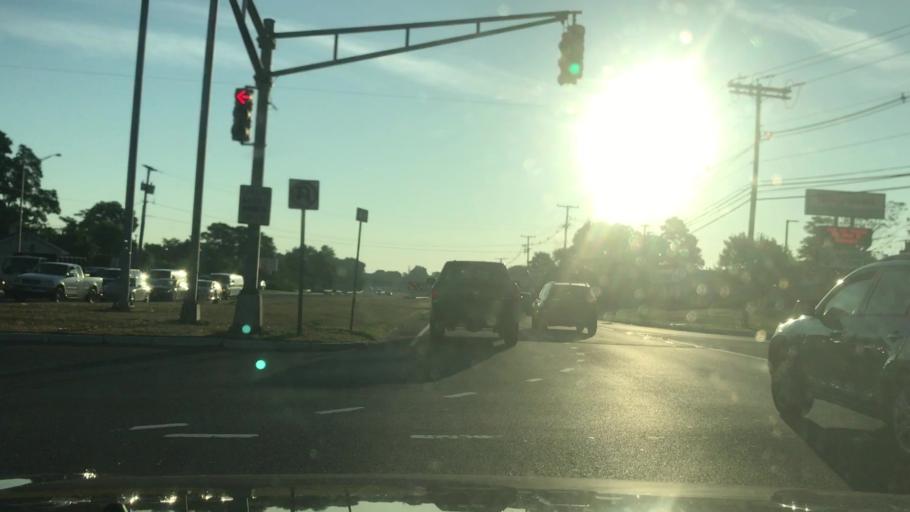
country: US
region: New Jersey
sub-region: Monmouth County
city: West Long Branch
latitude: 40.2954
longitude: -74.0290
